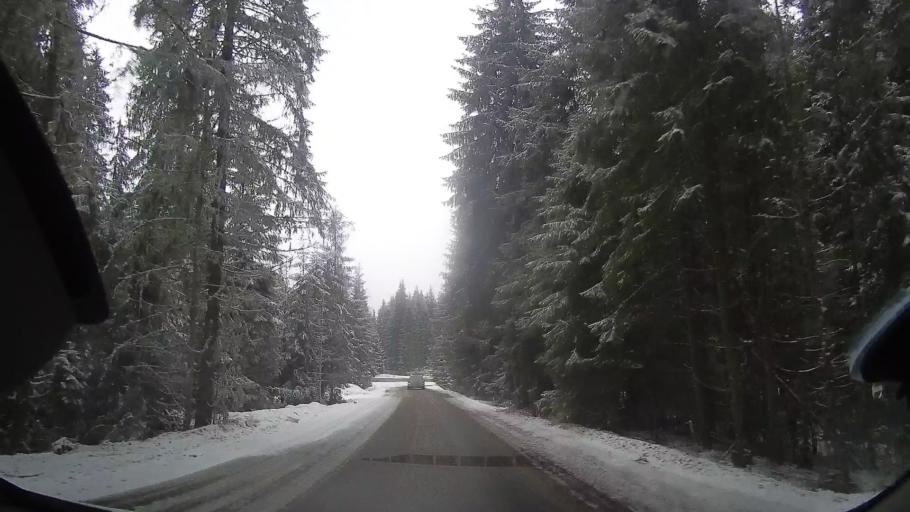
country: RO
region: Cluj
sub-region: Comuna Belis
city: Belis
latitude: 46.6507
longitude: 23.0405
